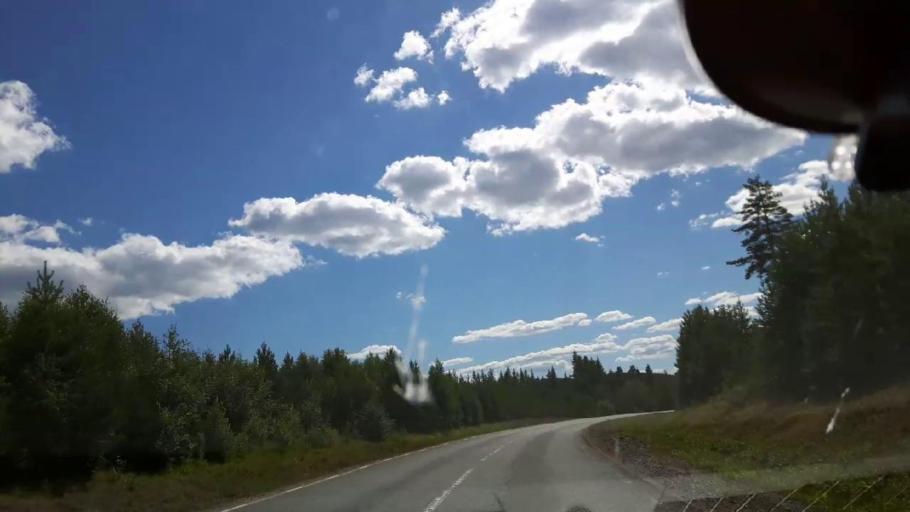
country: SE
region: Jaemtland
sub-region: Ragunda Kommun
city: Hammarstrand
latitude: 62.8623
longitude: 16.2150
